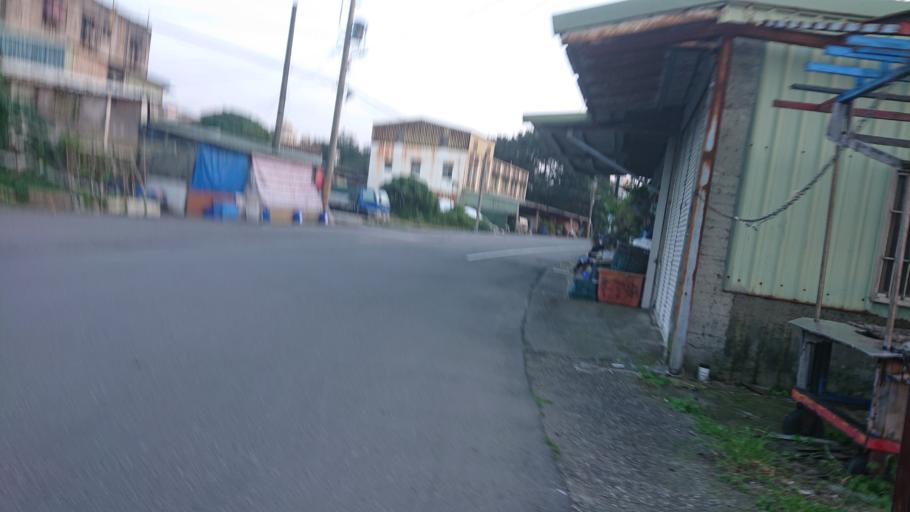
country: TW
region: Taipei
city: Taipei
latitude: 25.1883
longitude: 121.4199
